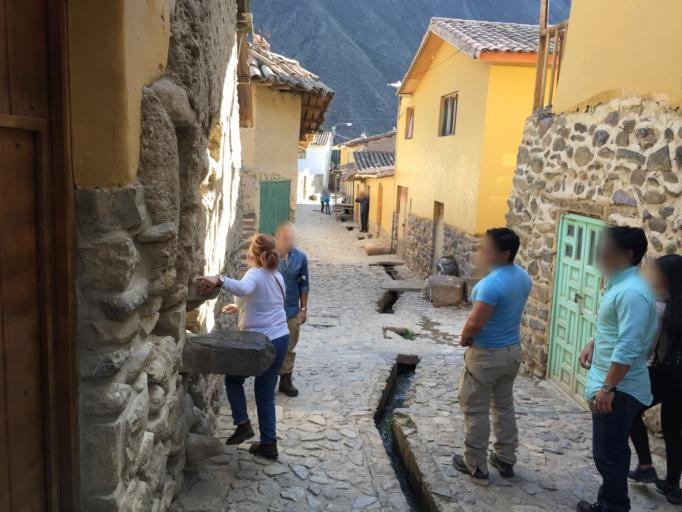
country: PE
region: Cusco
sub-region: Provincia de Urubamba
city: Ollantaytambo
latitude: -13.2581
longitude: -72.2656
